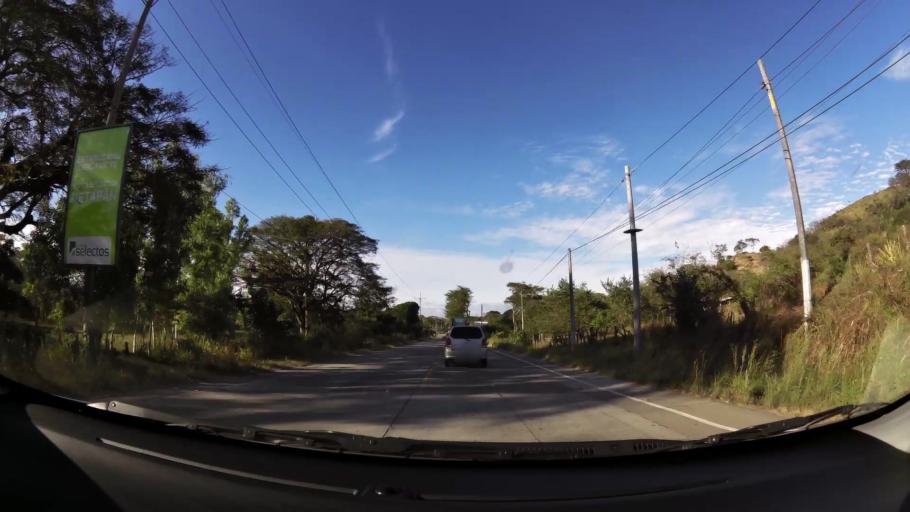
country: SV
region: Santa Ana
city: Metapan
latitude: 14.2793
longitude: -89.4612
